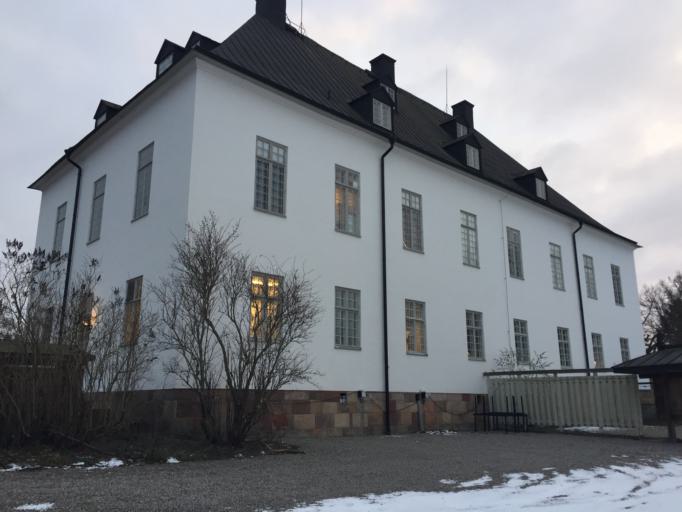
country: SE
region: Stockholm
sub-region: Haninge Kommun
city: Haninge
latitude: 59.1079
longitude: 18.1939
